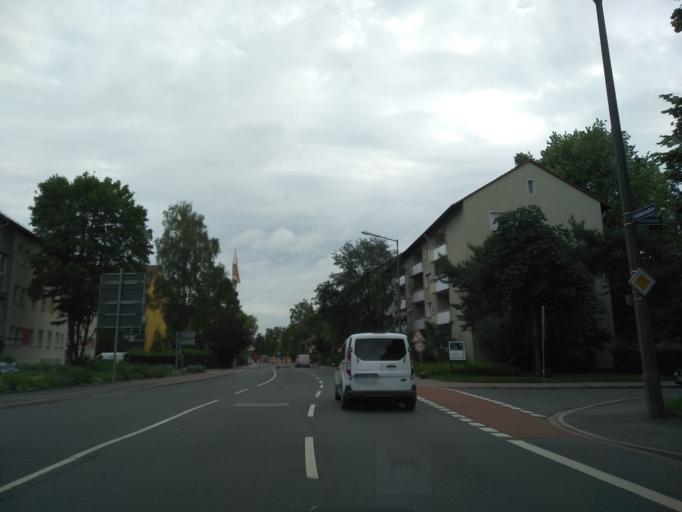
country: DE
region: Bavaria
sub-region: Regierungsbezirk Mittelfranken
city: Erlangen
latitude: 49.5784
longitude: 11.0049
